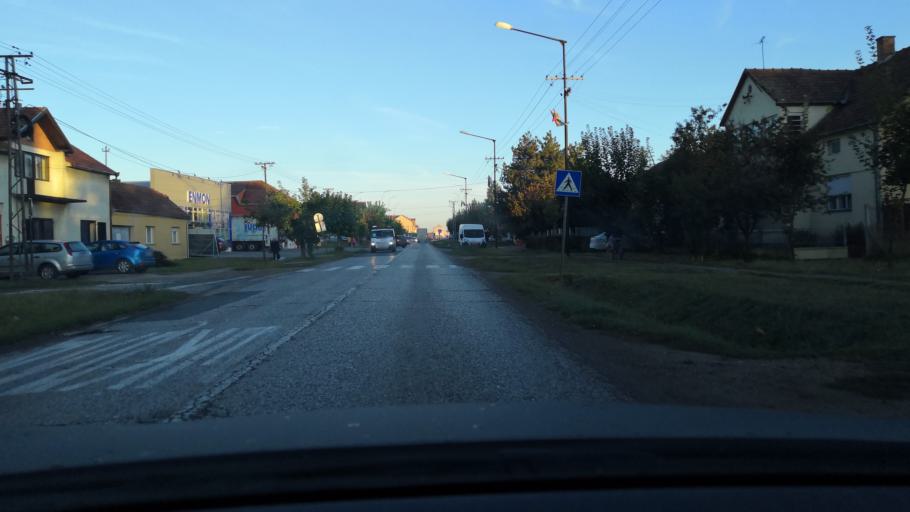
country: RS
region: Autonomna Pokrajina Vojvodina
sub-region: Sremski Okrug
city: Ingija
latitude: 45.0387
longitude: 20.0907
